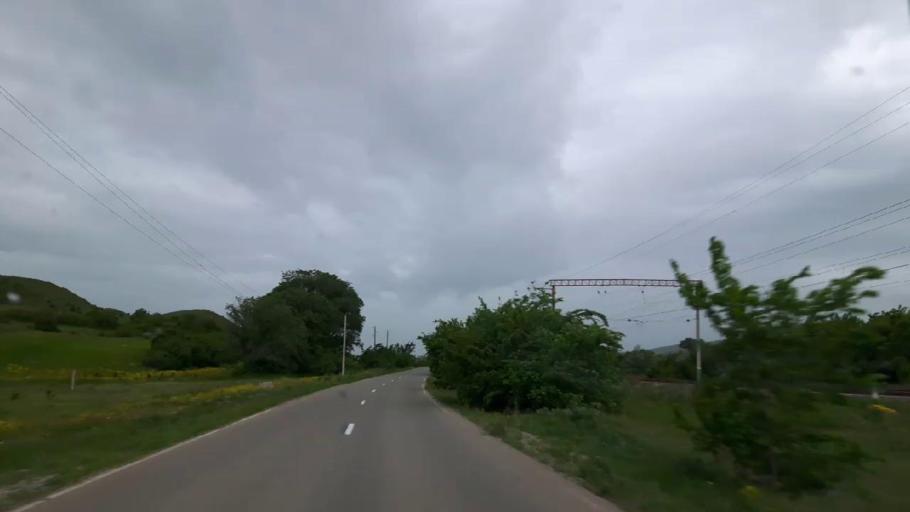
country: GE
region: Shida Kartli
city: Gori
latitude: 41.9948
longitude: 44.0263
